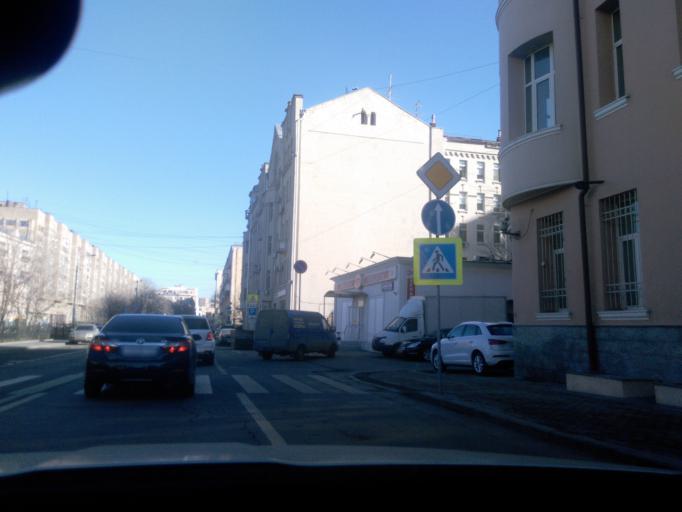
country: RU
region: Moskovskaya
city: Dorogomilovo
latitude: 55.7381
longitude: 37.5760
